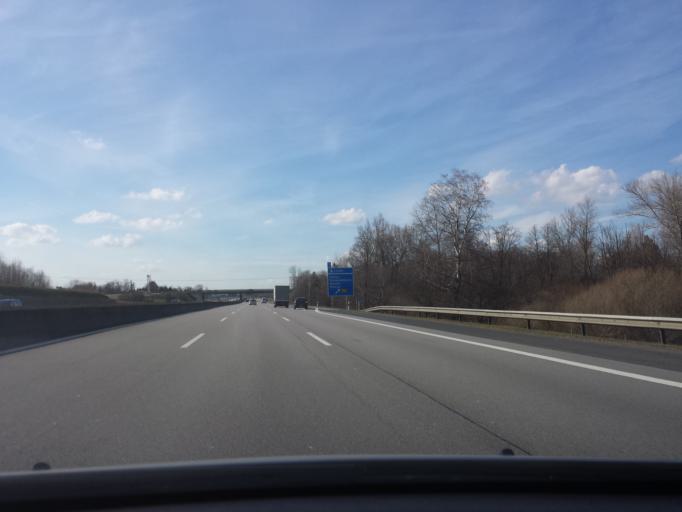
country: DE
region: Bavaria
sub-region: Upper Bavaria
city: Bergkirchen
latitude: 48.2310
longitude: 11.3527
